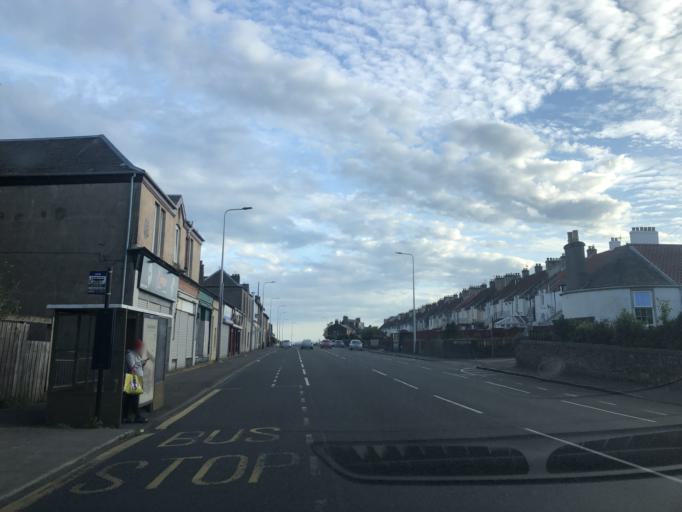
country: GB
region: Scotland
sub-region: Fife
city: Buckhaven
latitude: 56.1802
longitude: -3.0216
